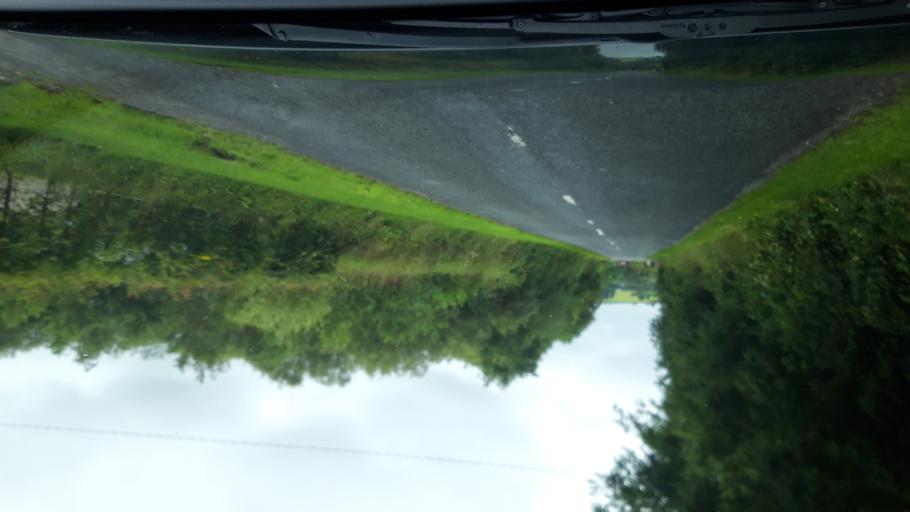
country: IE
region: Munster
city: Cahir
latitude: 52.1796
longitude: -7.8493
